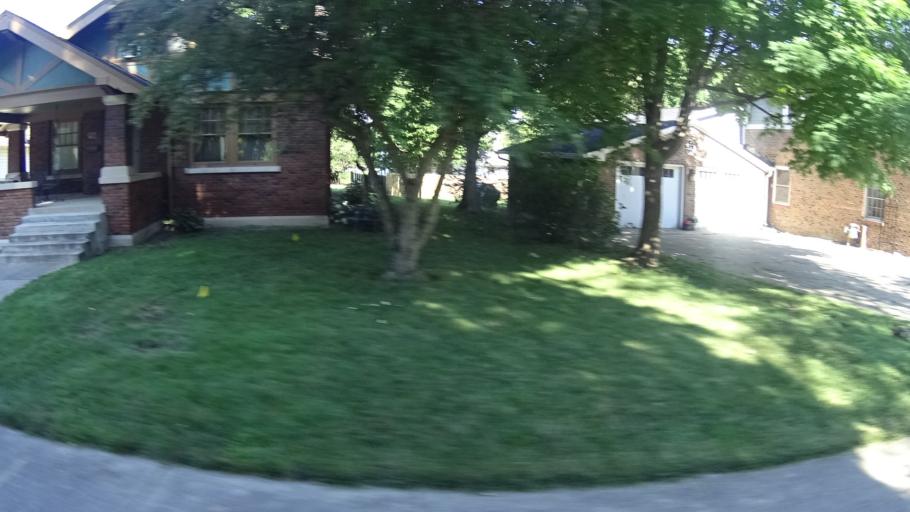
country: US
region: Indiana
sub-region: Madison County
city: Pendleton
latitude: 39.9979
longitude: -85.7463
